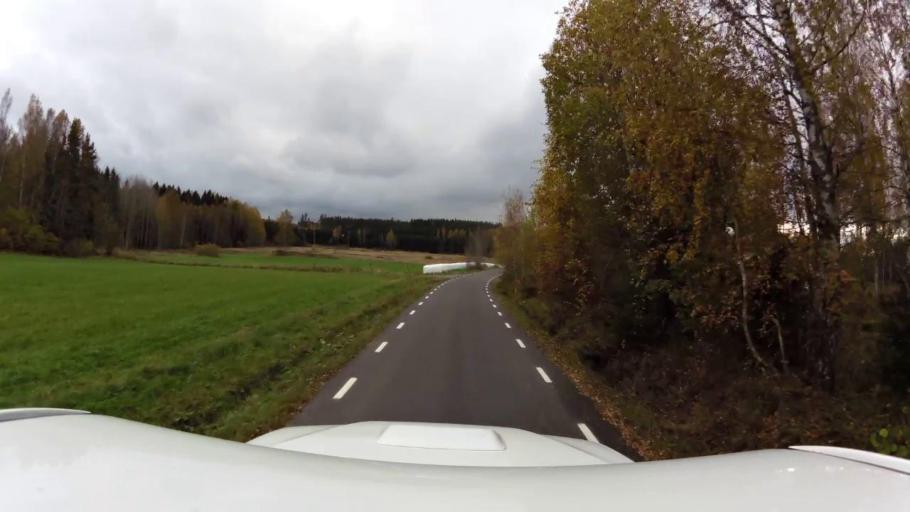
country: SE
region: OEstergoetland
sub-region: Linkopings Kommun
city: Ljungsbro
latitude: 58.5721
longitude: 15.4616
